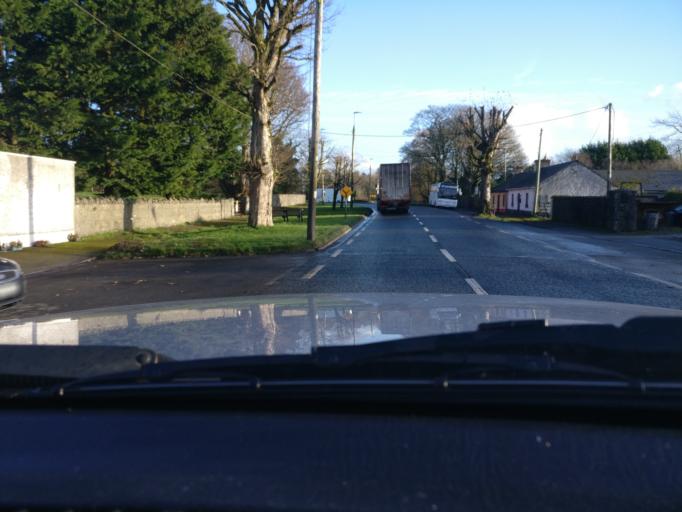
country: IE
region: Leinster
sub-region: An Mhi
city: Athboy
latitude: 53.6630
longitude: -7.0121
